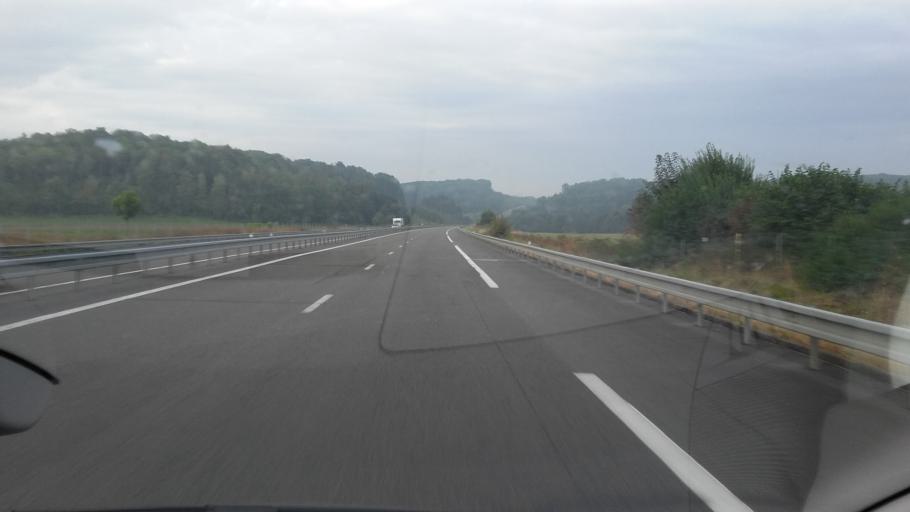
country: FR
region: Champagne-Ardenne
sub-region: Departement des Ardennes
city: Attigny
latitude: 49.6219
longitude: 4.5491
